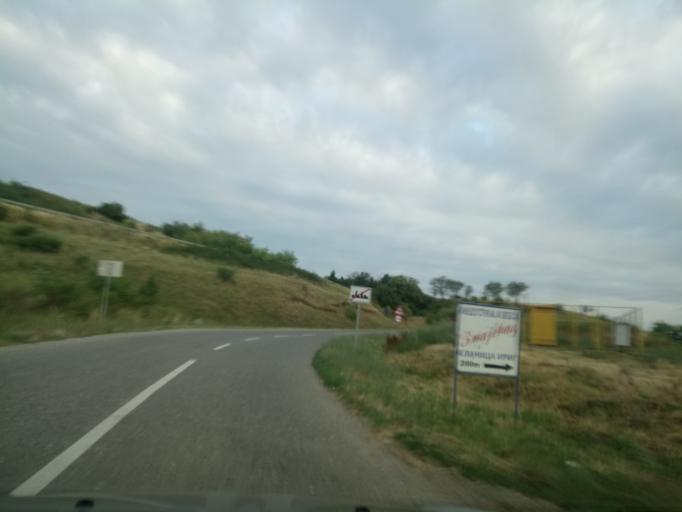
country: RS
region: Autonomna Pokrajina Vojvodina
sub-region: Sremski Okrug
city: Irig
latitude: 45.0941
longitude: 19.8659
